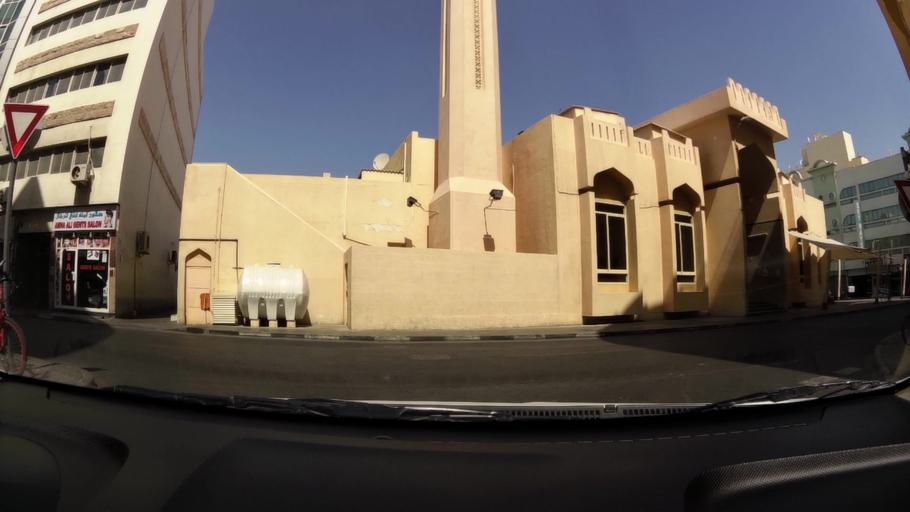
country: AE
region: Ash Shariqah
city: Sharjah
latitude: 25.2781
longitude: 55.3129
